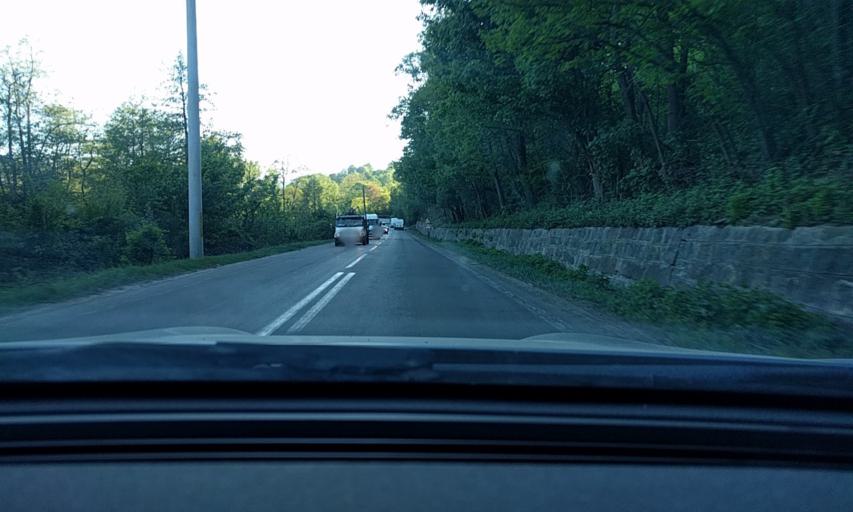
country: RO
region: Bacau
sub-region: Oras Slanic-Moldova
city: Slanic-Moldova
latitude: 46.1923
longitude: 26.5079
